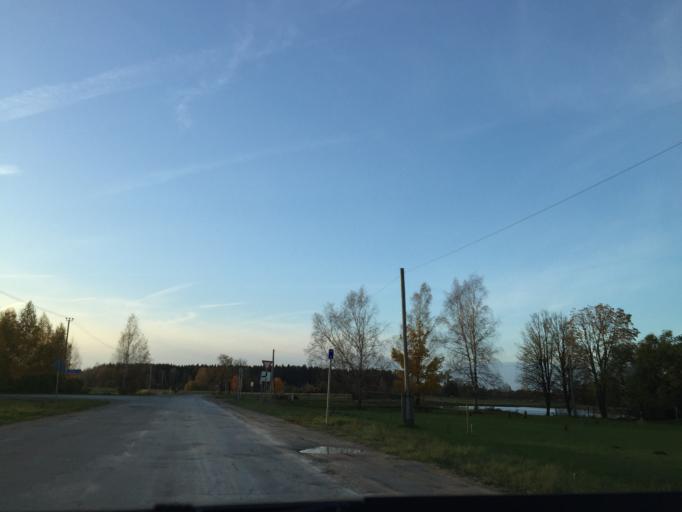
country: LV
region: Malpils
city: Malpils
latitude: 56.8931
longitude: 24.9337
